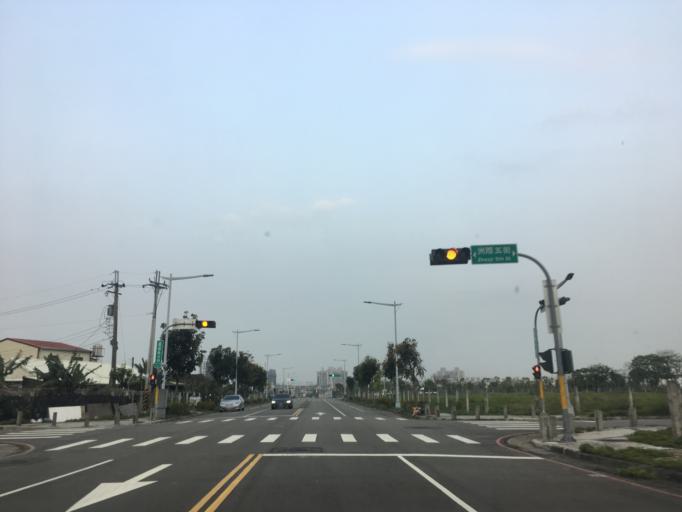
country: TW
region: Taiwan
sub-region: Taichung City
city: Taichung
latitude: 24.1954
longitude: 120.6719
